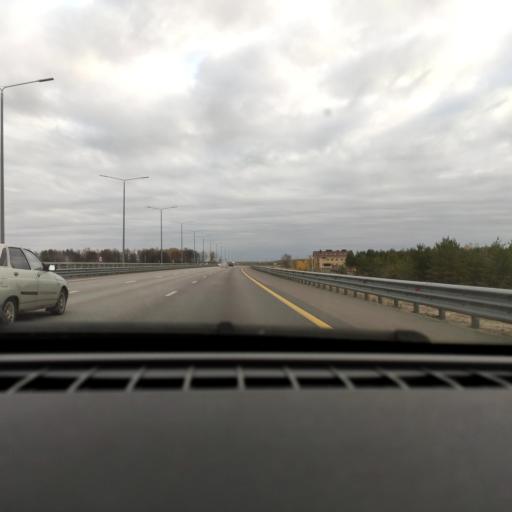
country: RU
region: Voronezj
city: Somovo
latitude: 51.7831
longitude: 39.2909
